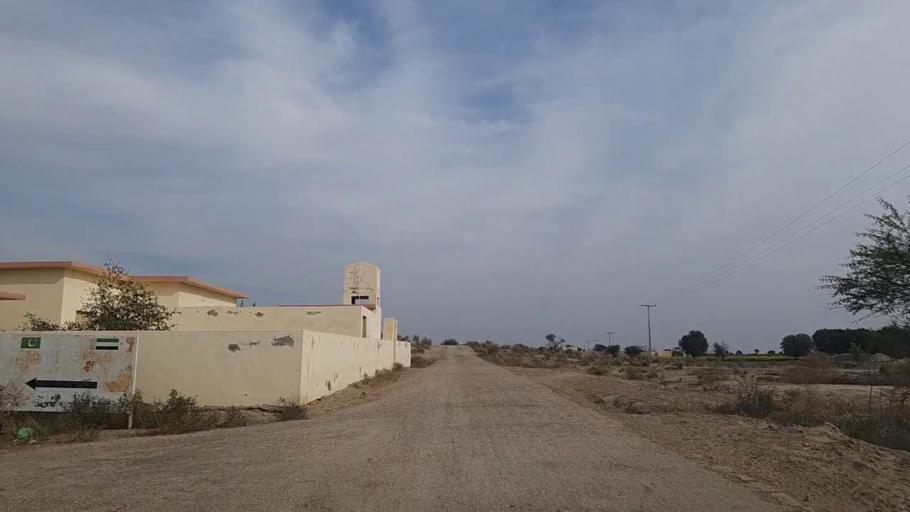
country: PK
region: Sindh
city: Jam Sahib
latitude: 26.4348
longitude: 68.6373
